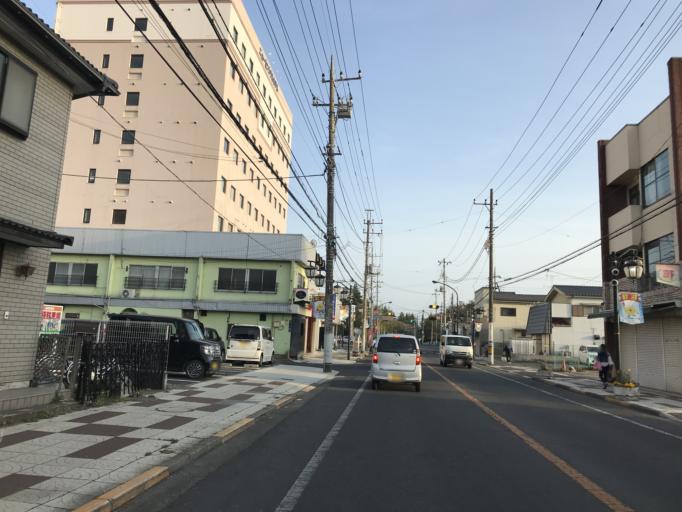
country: JP
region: Ibaraki
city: Katsuta
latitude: 36.3872
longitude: 140.5273
